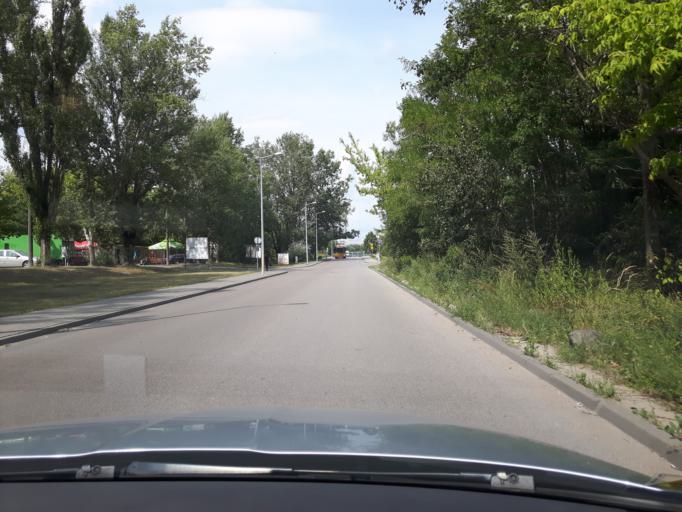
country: PL
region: Masovian Voivodeship
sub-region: Warszawa
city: Wlochy
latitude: 52.1530
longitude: 20.9946
